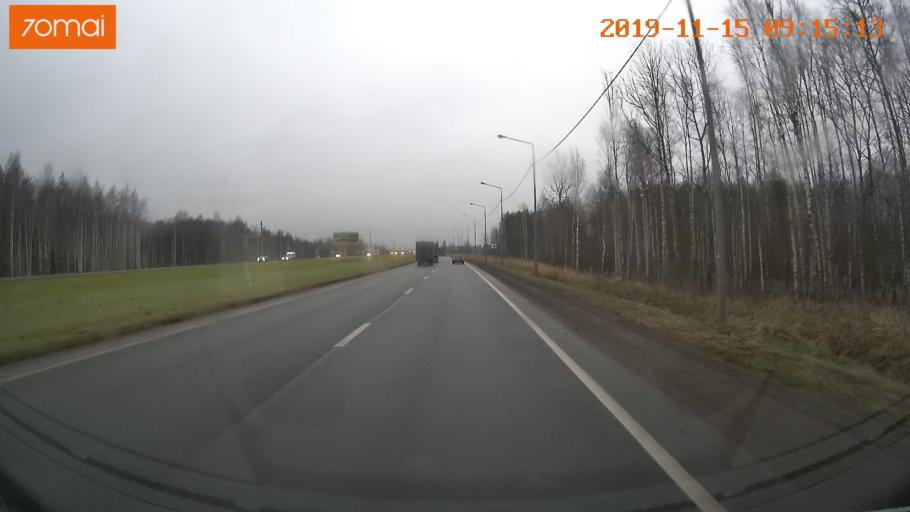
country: RU
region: Vologda
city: Tonshalovo
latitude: 59.2361
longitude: 37.9653
